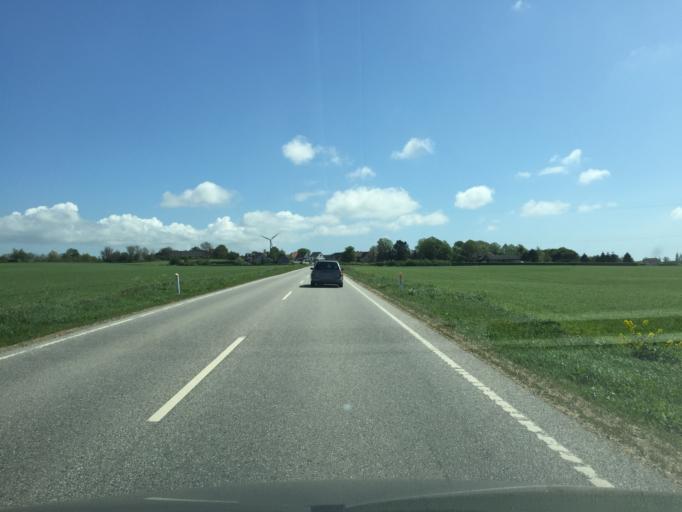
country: DK
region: Zealand
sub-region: Vordingborg Kommune
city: Stege
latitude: 54.9672
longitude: 12.2253
